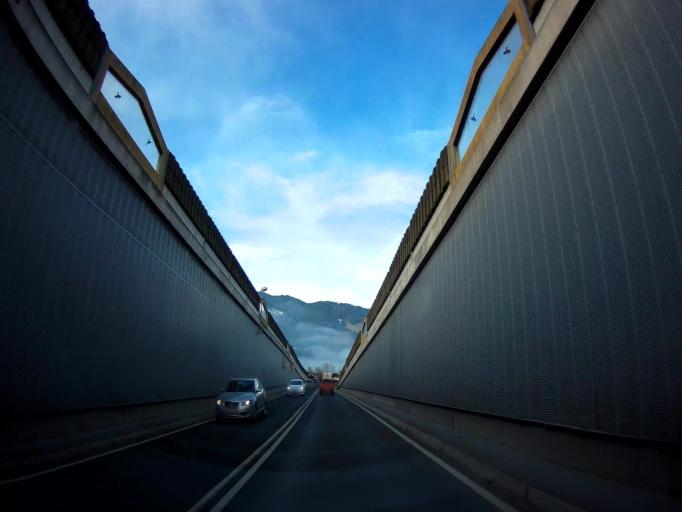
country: AT
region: Salzburg
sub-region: Politischer Bezirk Zell am See
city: Maishofen
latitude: 47.3703
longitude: 12.8055
